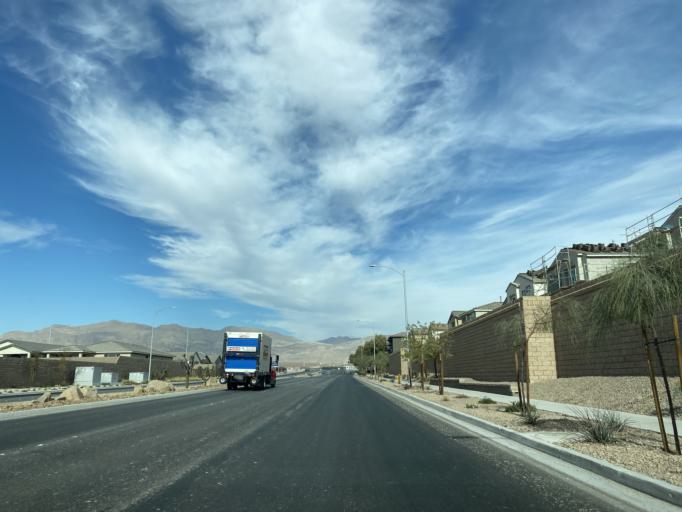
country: US
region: Nevada
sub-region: Clark County
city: Nellis Air Force Base
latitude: 36.2805
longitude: -115.1168
